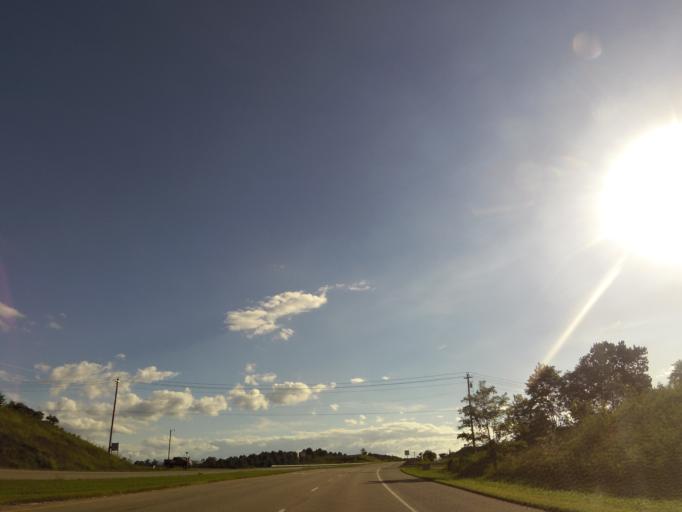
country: US
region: Tennessee
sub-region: Cocke County
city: Newport
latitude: 36.0213
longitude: -83.0377
